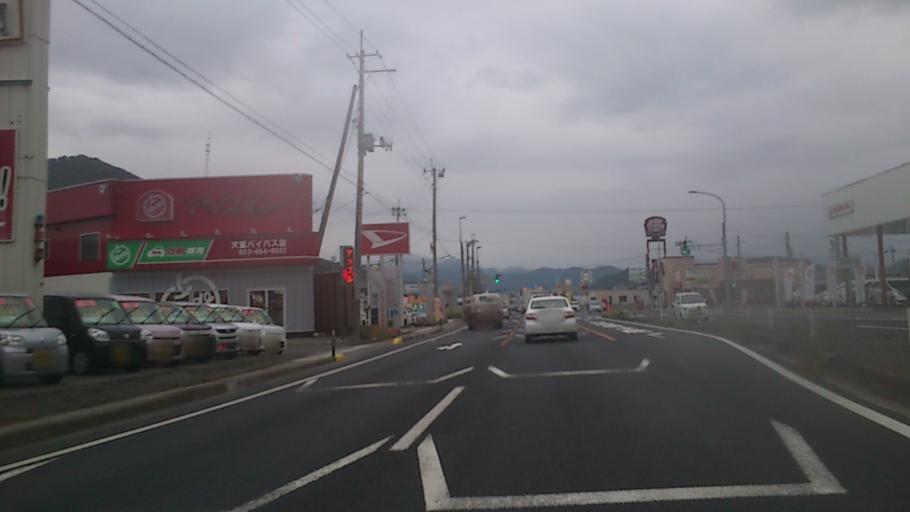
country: JP
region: Yamagata
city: Tendo
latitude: 38.3701
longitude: 140.3842
